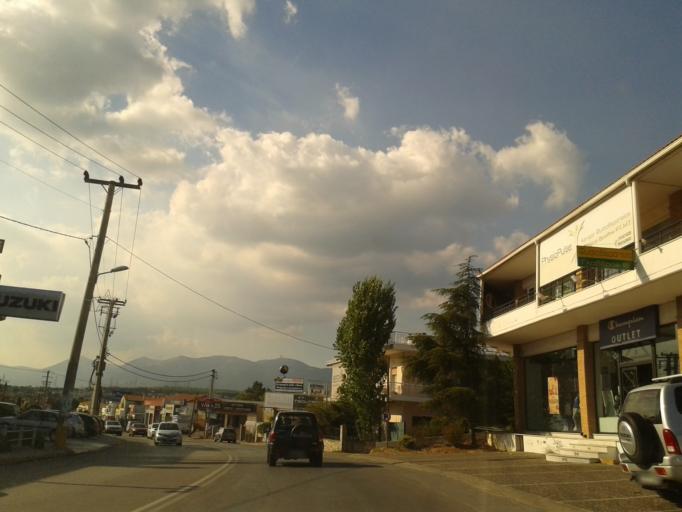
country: GR
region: Attica
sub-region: Nomarchia Anatolikis Attikis
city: Agios Stefanos
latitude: 38.1394
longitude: 23.8537
